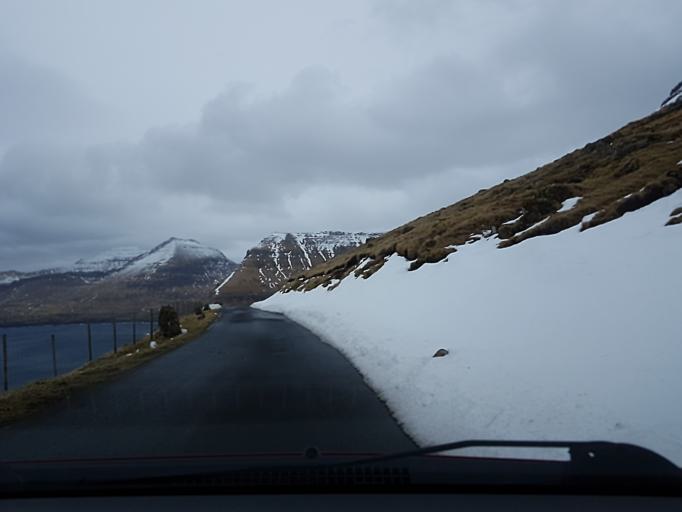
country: FO
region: Streymoy
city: Kollafjordhur
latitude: 62.0088
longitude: -6.9094
